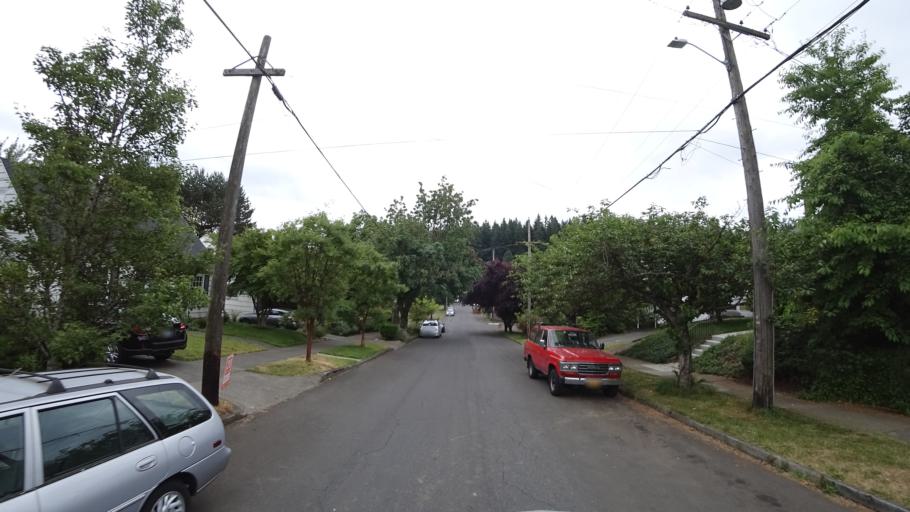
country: US
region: Oregon
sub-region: Multnomah County
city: Lents
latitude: 45.5181
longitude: -122.5922
